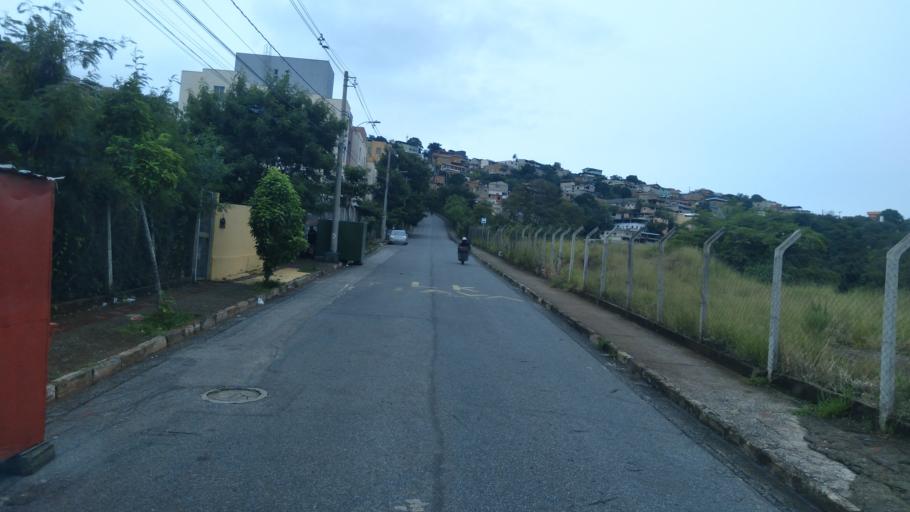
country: BR
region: Minas Gerais
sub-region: Belo Horizonte
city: Belo Horizonte
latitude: -19.9113
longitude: -43.8835
